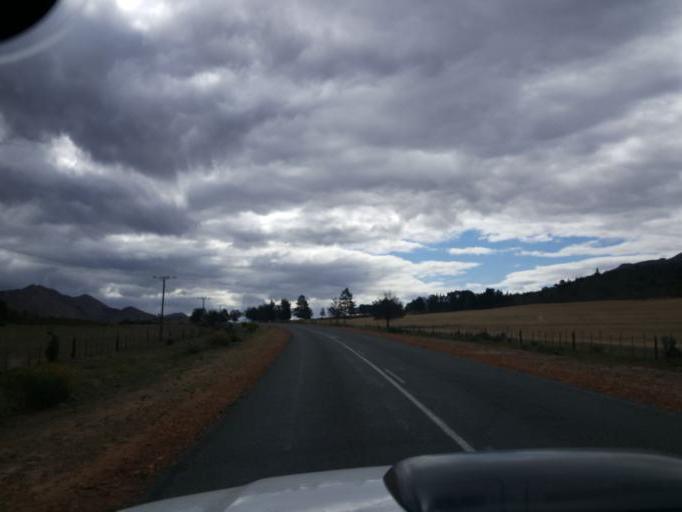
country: ZA
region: Western Cape
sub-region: Eden District Municipality
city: George
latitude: -33.8270
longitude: 22.4126
